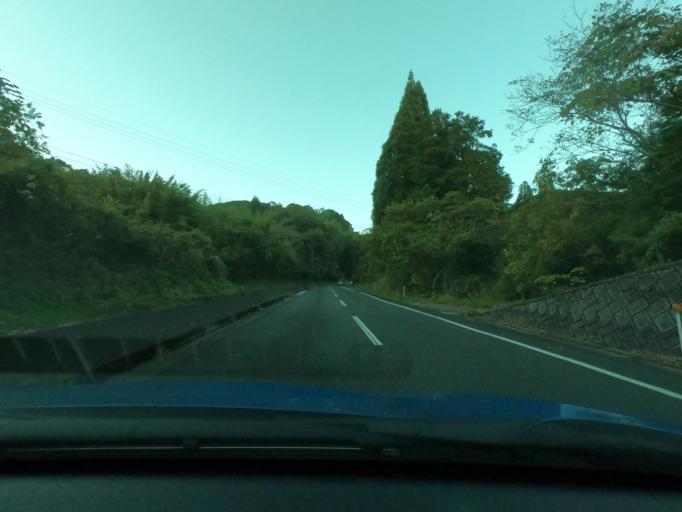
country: JP
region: Kagoshima
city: Satsumasendai
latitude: 31.8152
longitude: 130.4833
